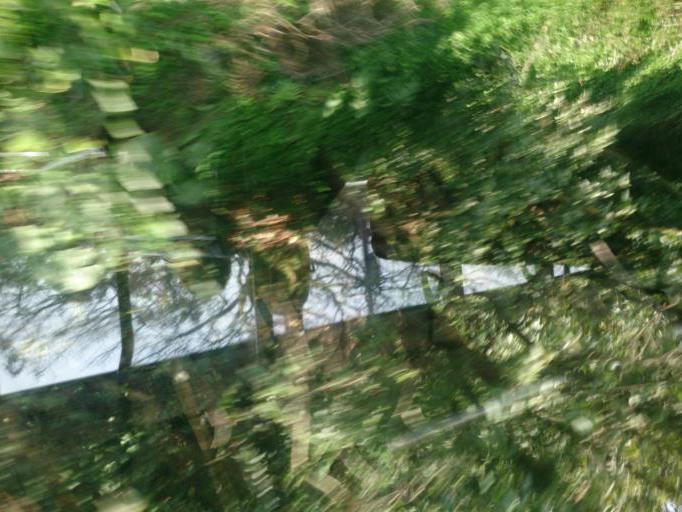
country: TW
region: Taipei
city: Taipei
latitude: 25.1796
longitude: 121.5438
